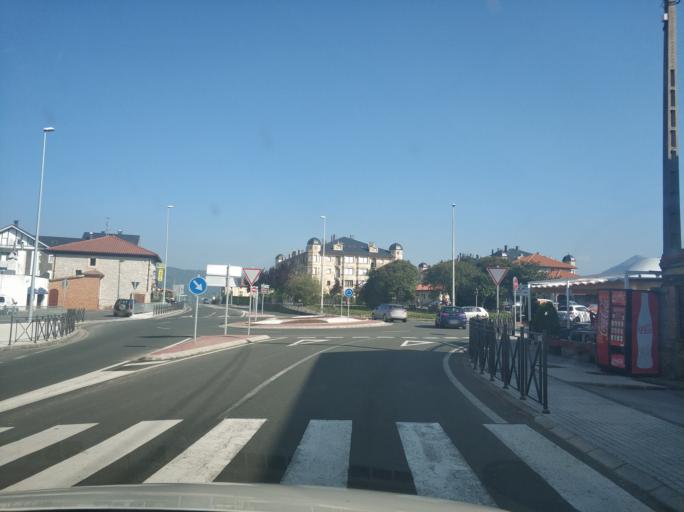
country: ES
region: Cantabria
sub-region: Provincia de Cantabria
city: Colindres
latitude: 43.3944
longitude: -3.4737
